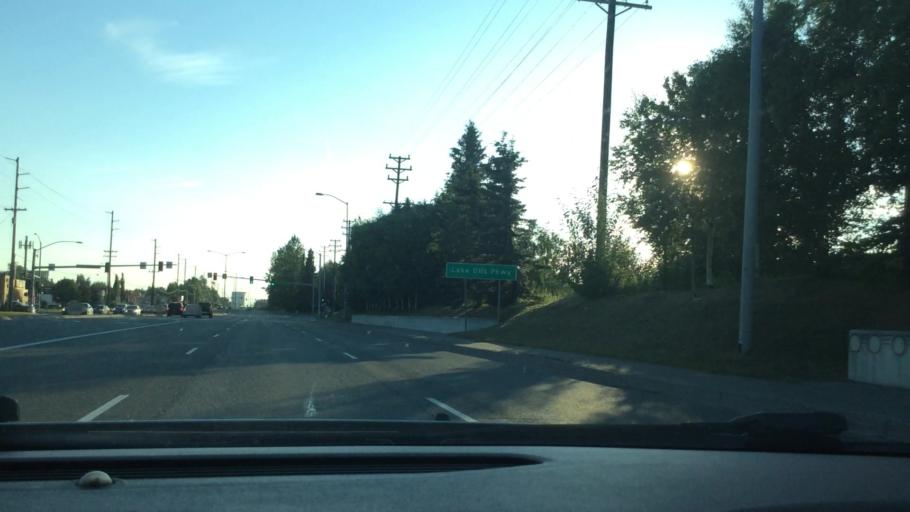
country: US
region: Alaska
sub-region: Anchorage Municipality
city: Anchorage
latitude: 61.1955
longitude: -149.8356
